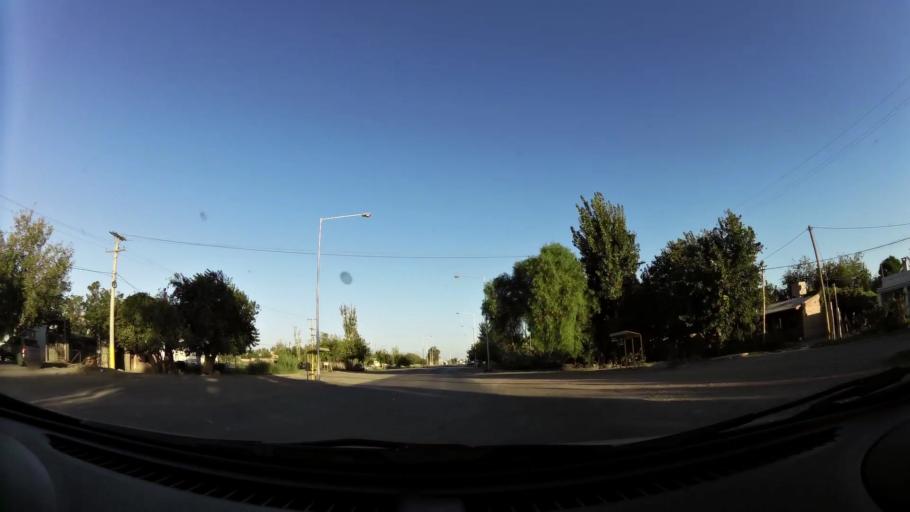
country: AR
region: San Juan
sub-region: Departamento de Santa Lucia
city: Santa Lucia
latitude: -31.5513
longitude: -68.4796
